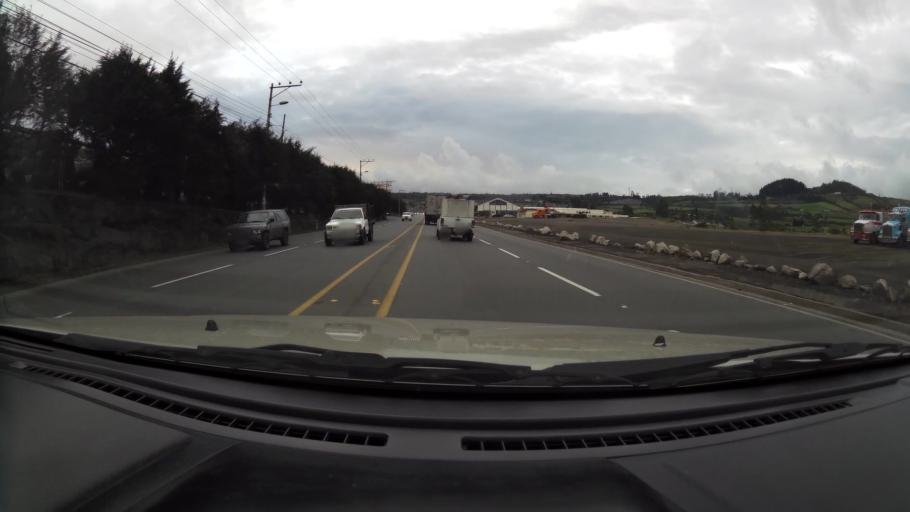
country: EC
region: Pichincha
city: Machachi
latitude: -0.4498
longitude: -78.6377
